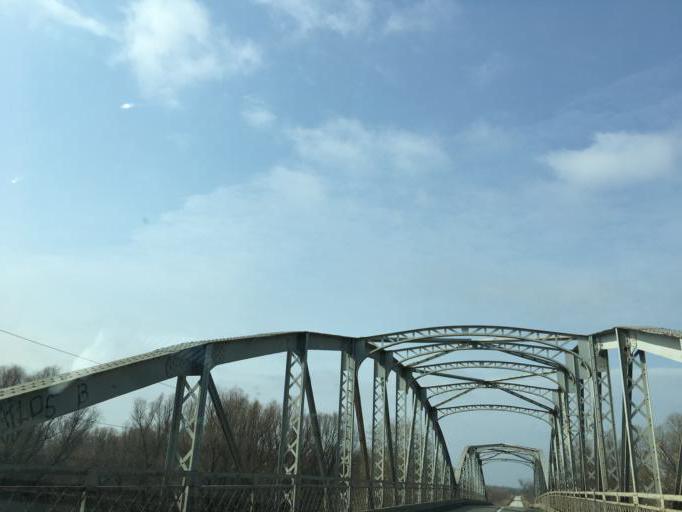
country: RS
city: Baranda
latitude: 45.0949
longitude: 20.4184
